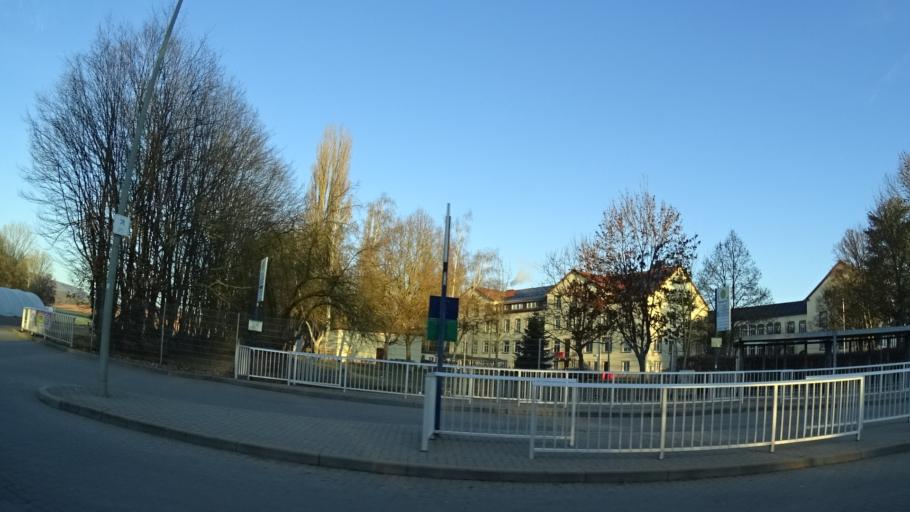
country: DE
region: Rheinland-Pfalz
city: Marnheim
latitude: 49.6338
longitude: 8.0284
